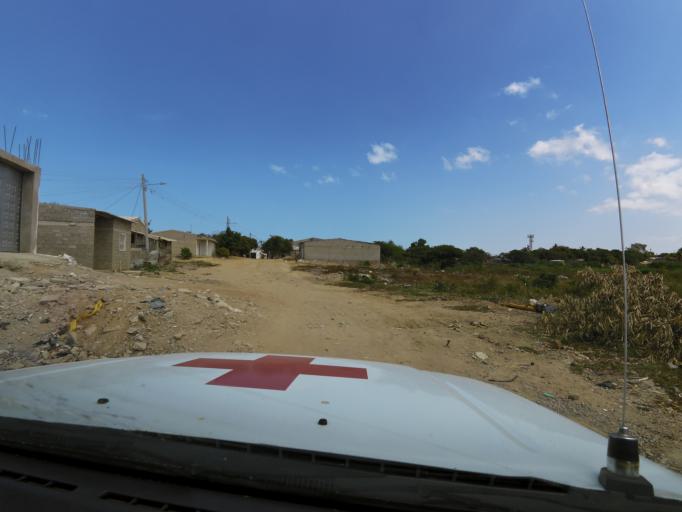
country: CO
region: La Guajira
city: Riohacha
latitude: 11.5304
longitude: -72.9075
